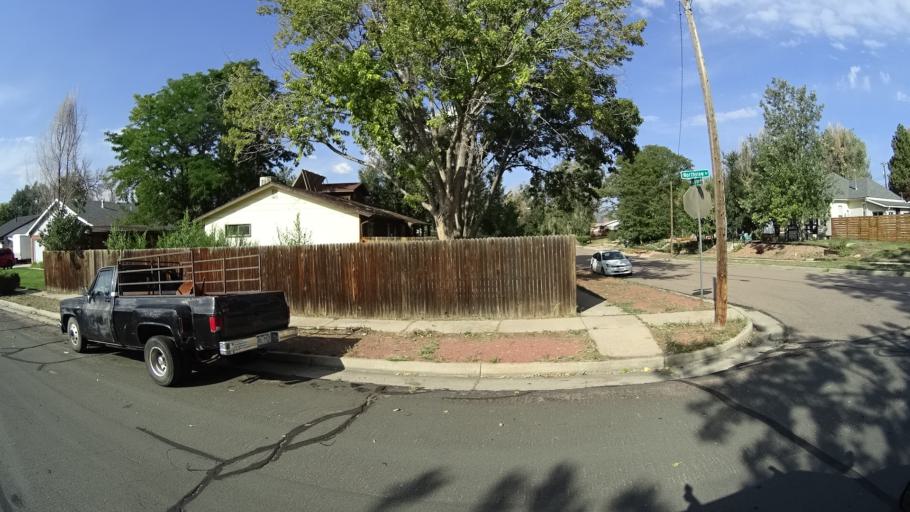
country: US
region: Colorado
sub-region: El Paso County
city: Colorado Springs
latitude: 38.8558
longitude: -104.7803
